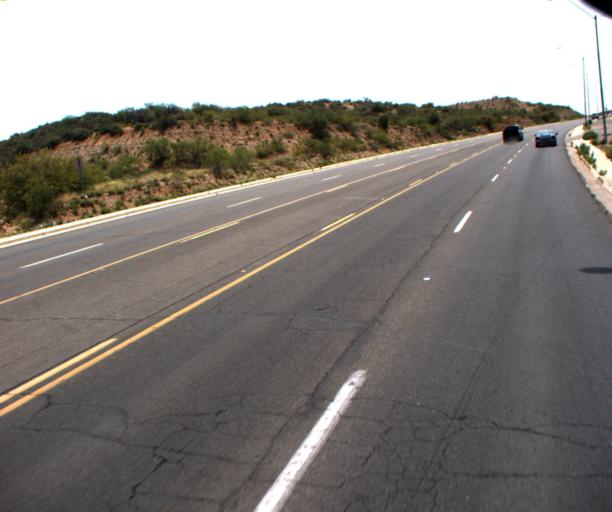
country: US
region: Arizona
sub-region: Gila County
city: Globe
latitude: 33.3909
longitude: -110.7639
